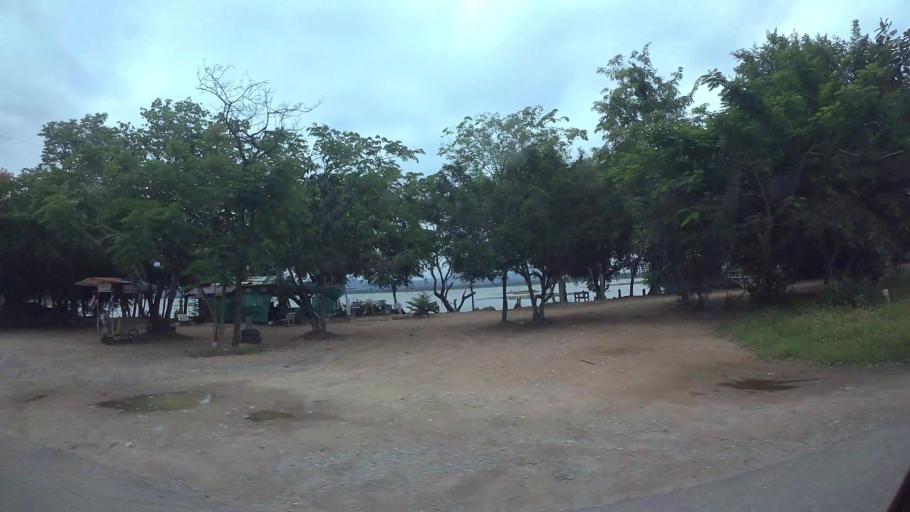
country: TH
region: Chon Buri
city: Si Racha
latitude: 13.1986
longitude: 100.9587
